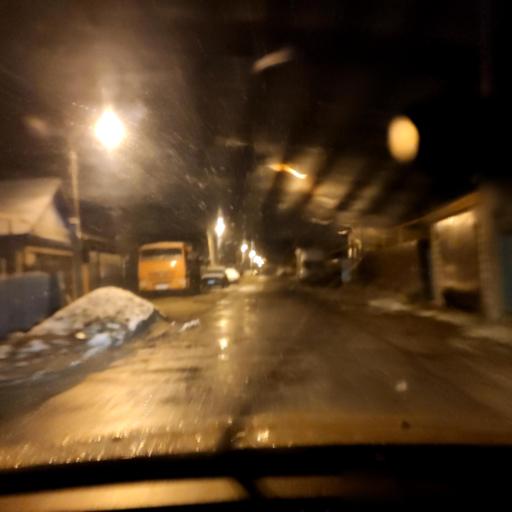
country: RU
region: Bashkortostan
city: Ufa
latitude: 54.7314
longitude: 55.9006
